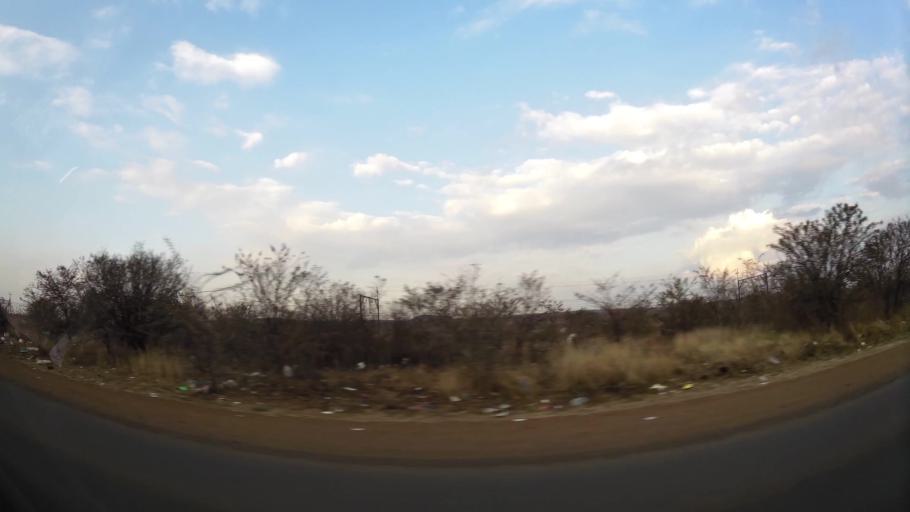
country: ZA
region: Gauteng
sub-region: City of Johannesburg Metropolitan Municipality
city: Orange Farm
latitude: -26.5843
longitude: 27.8548
